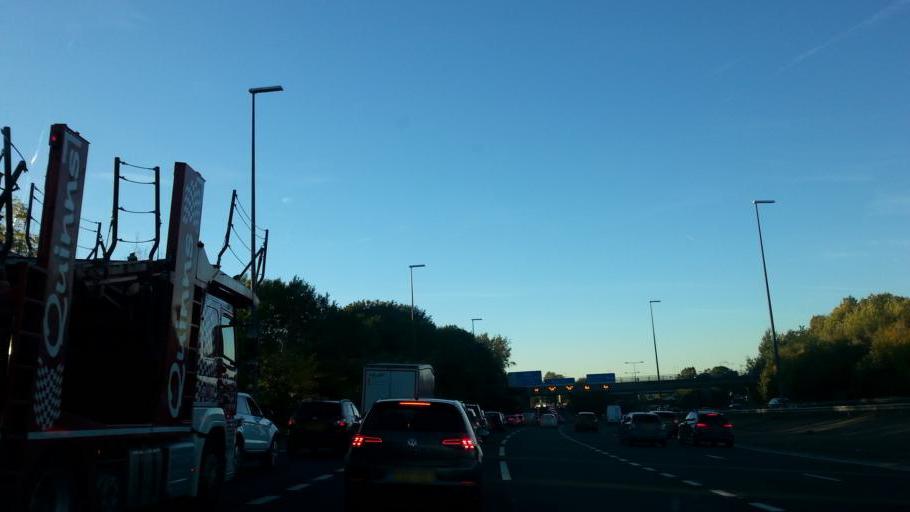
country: GB
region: England
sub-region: Borough of Bury
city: Prestwich
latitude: 53.5464
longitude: -2.2564
